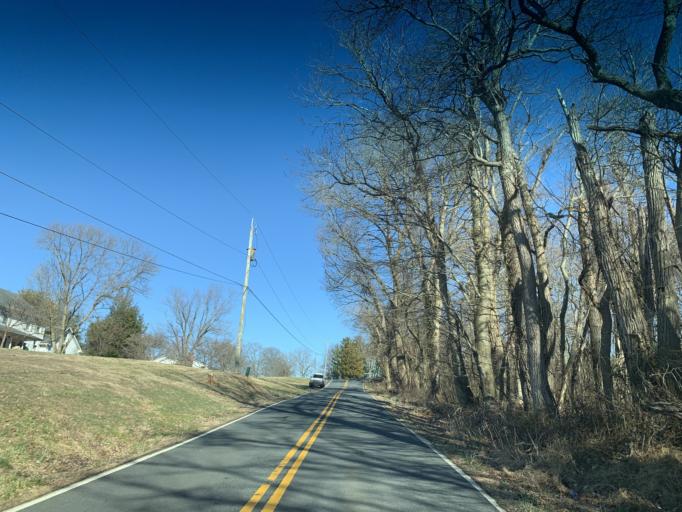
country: US
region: Maryland
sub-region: Cecil County
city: Rising Sun
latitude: 39.6659
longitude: -76.1333
